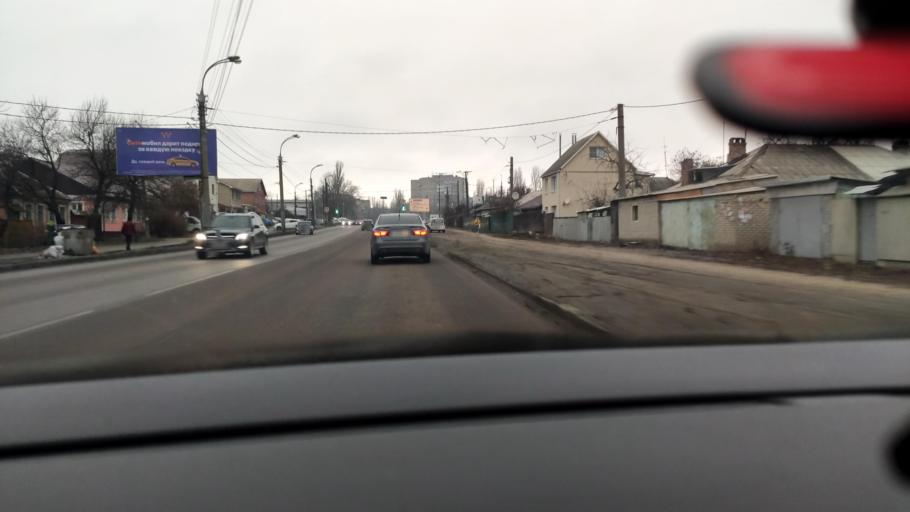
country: RU
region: Voronezj
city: Voronezh
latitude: 51.6429
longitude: 39.1556
